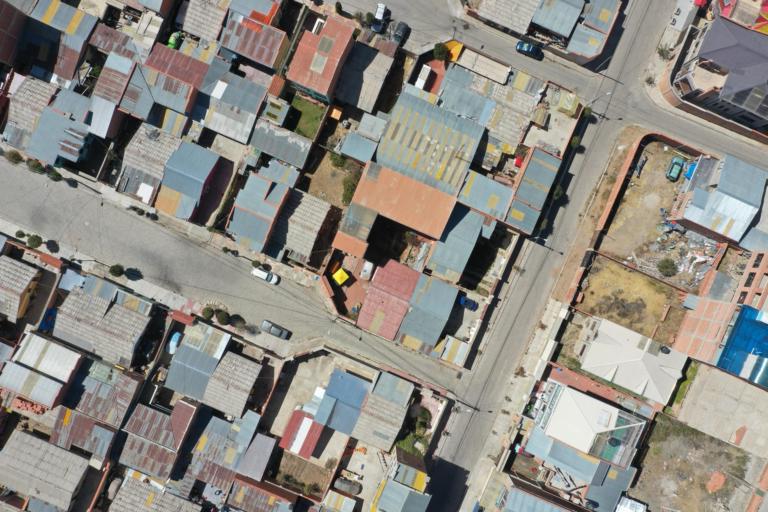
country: BO
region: La Paz
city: La Paz
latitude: -16.5337
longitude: -68.1527
